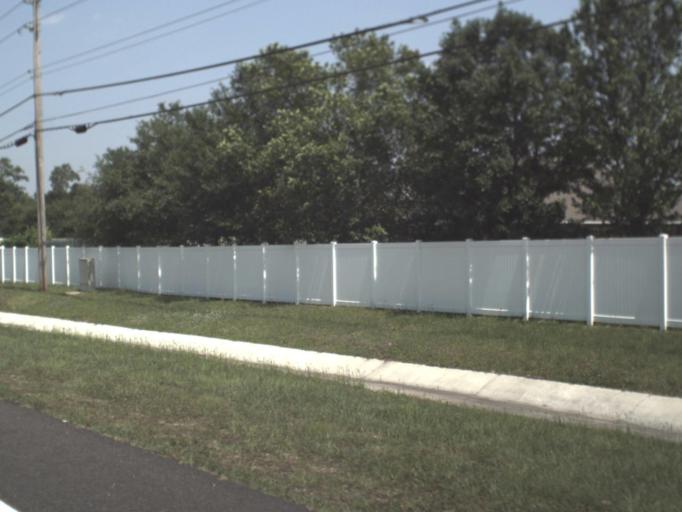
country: US
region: Florida
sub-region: Clay County
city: Bellair-Meadowbrook Terrace
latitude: 30.2721
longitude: -81.8381
